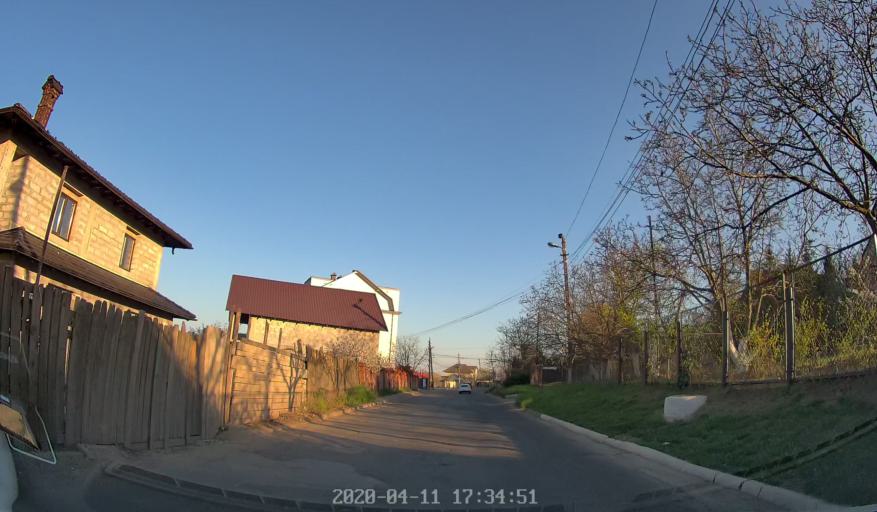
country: MD
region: Laloveni
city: Ialoveni
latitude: 46.9933
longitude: 28.8022
